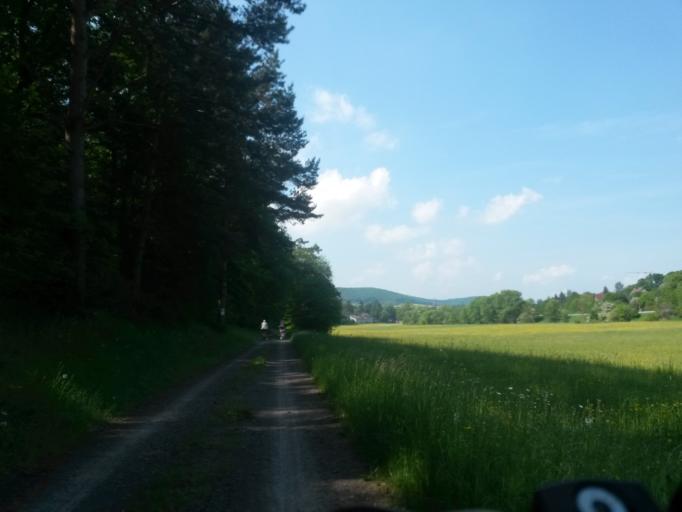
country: DE
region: Bavaria
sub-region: Regierungsbezirk Unterfranken
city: Euerdorf
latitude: 50.1550
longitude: 10.0348
